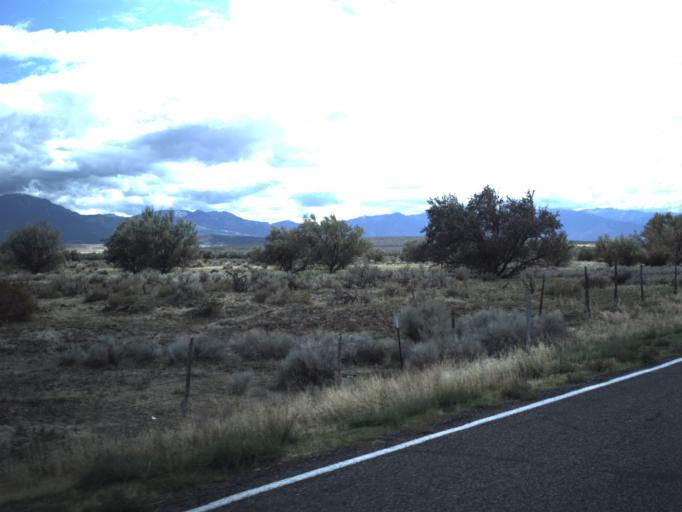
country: US
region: Utah
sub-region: Millard County
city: Fillmore
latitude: 39.0983
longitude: -112.4101
